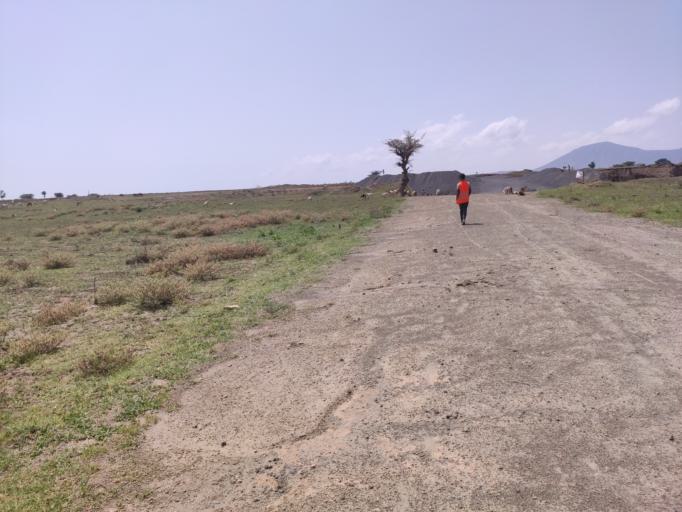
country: ET
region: Oromiya
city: Mojo
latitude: 8.3152
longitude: 38.9511
